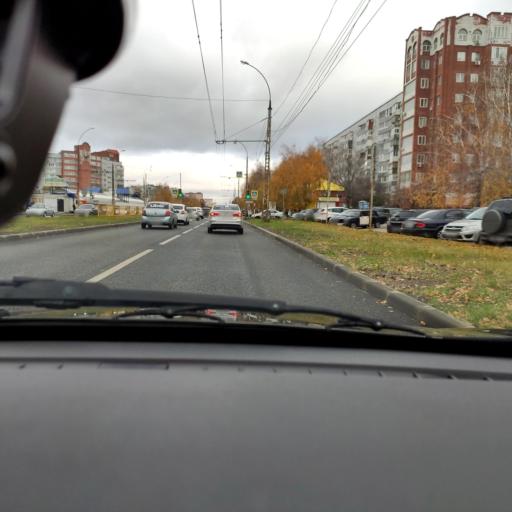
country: RU
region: Samara
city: Tol'yatti
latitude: 53.5288
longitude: 49.3276
